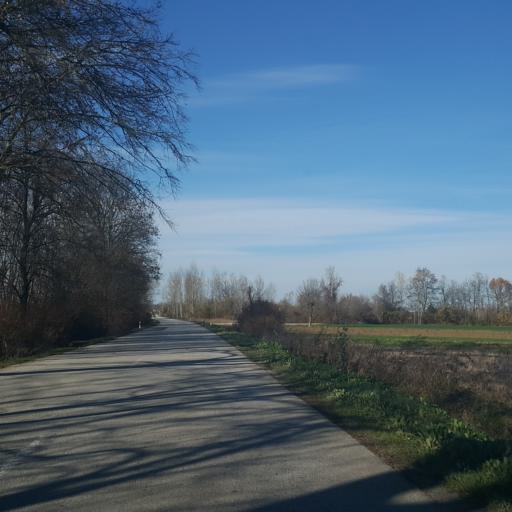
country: RS
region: Central Serbia
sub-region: Sumadijski Okrug
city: Topola
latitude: 44.2546
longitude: 20.8278
